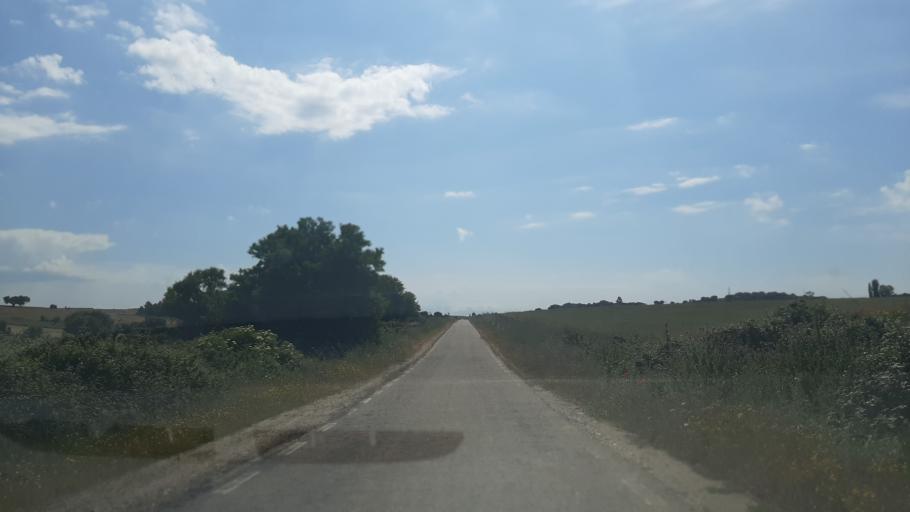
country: ES
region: Castille and Leon
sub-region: Provincia de Salamanca
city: Aldea del Obispo
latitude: 40.6534
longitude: -6.7711
